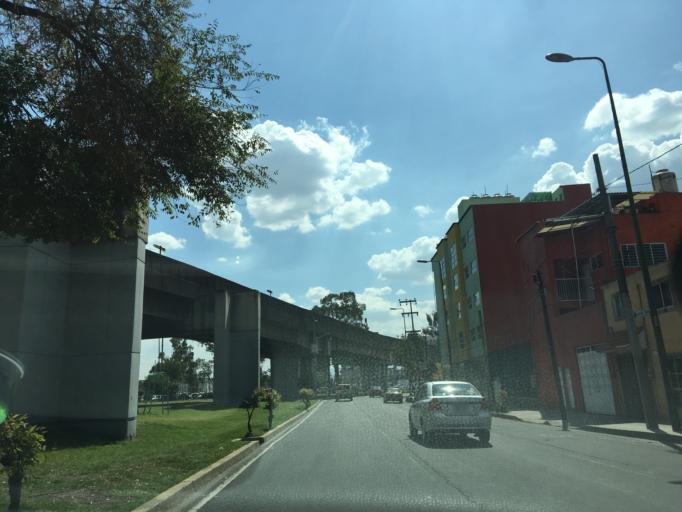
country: MX
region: Mexico City
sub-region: Iztacalco
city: Iztacalco
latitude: 19.4084
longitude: -99.0776
